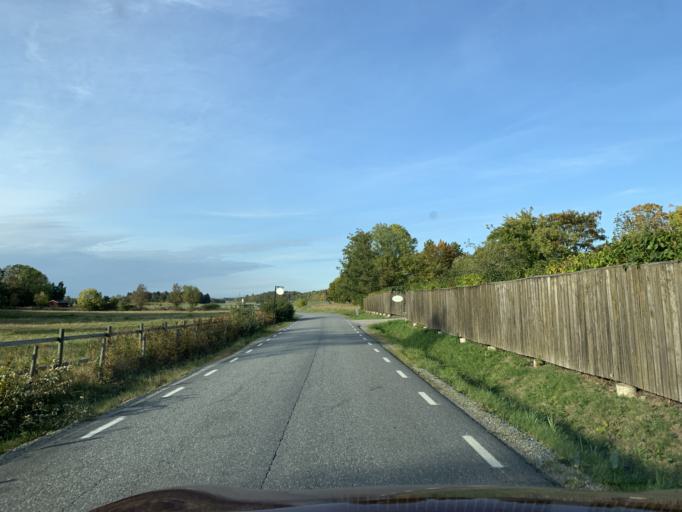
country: SE
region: Stockholm
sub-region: Upplands-Bro Kommun
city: Bro
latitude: 59.5049
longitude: 17.5856
